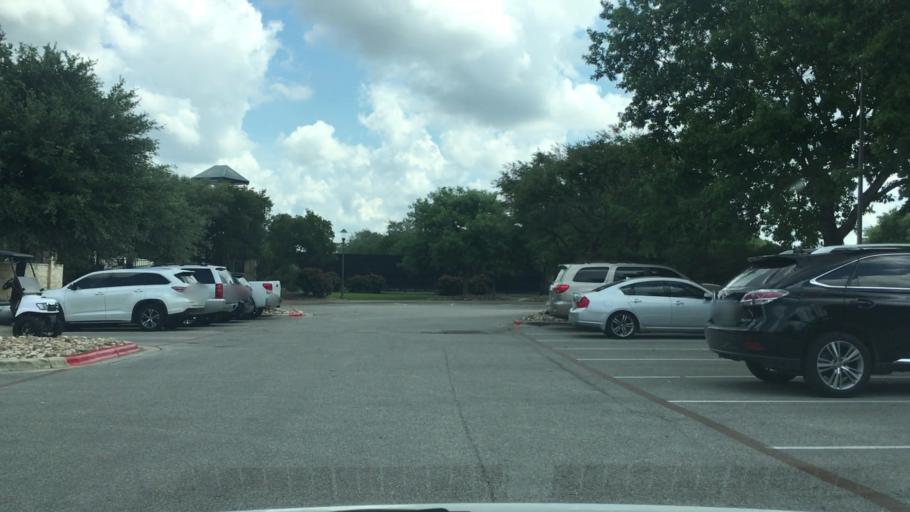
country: US
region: Texas
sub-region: Williamson County
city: Anderson Mill
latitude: 30.4619
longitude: -97.8567
